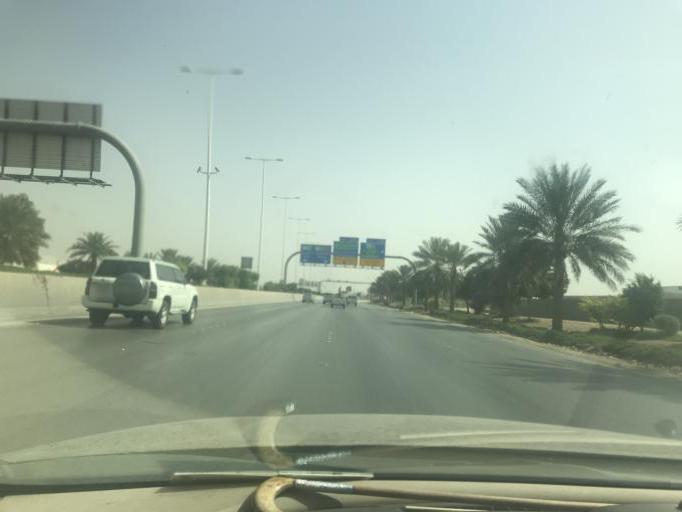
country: SA
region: Ar Riyad
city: Riyadh
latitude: 24.7319
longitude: 46.7090
